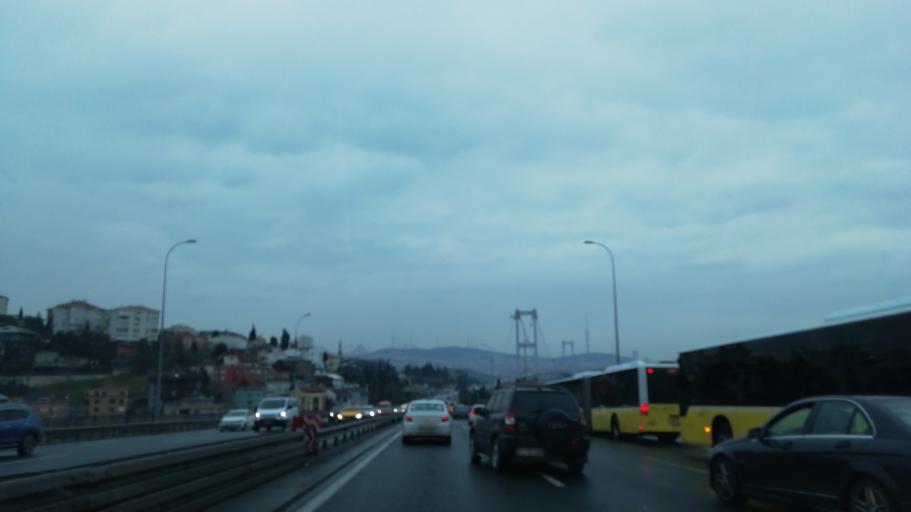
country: TR
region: Istanbul
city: UEskuedar
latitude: 41.0562
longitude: 29.0213
